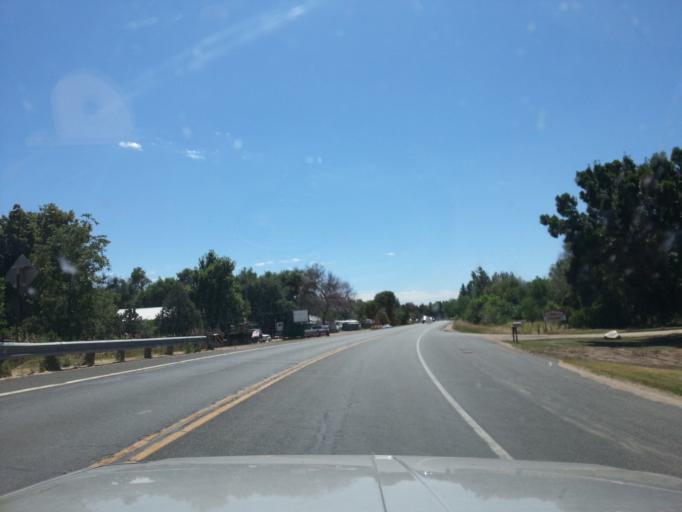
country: US
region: Colorado
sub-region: Larimer County
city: Loveland
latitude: 40.4190
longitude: -105.1771
